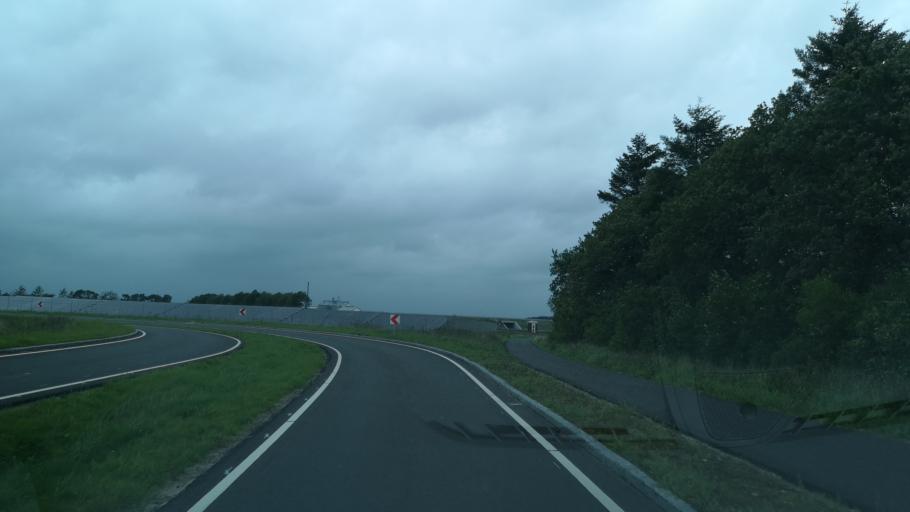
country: DK
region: Central Jutland
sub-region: Herning Kommune
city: Snejbjerg
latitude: 56.1604
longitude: 8.8904
